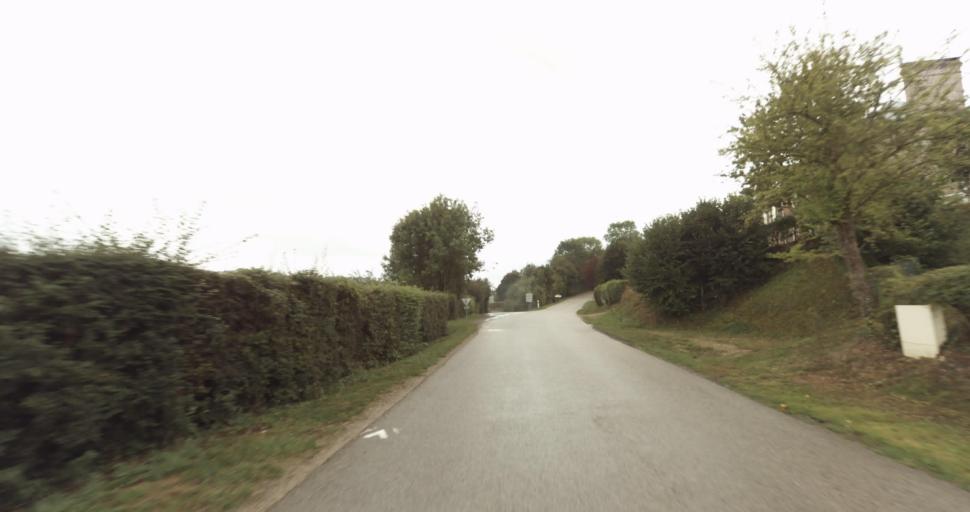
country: FR
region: Lower Normandy
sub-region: Departement de l'Orne
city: Vimoutiers
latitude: 48.9069
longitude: 0.2074
